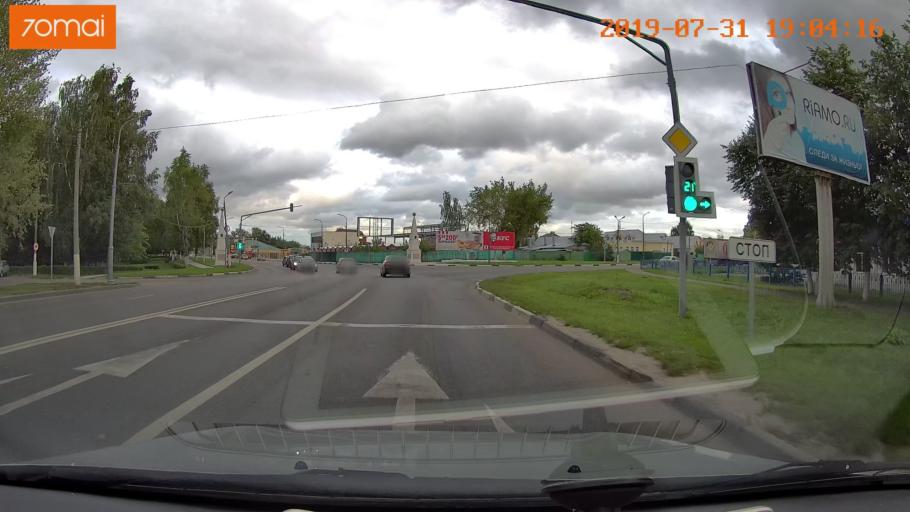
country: RU
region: Moskovskaya
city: Raduzhnyy
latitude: 55.1096
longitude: 38.7401
